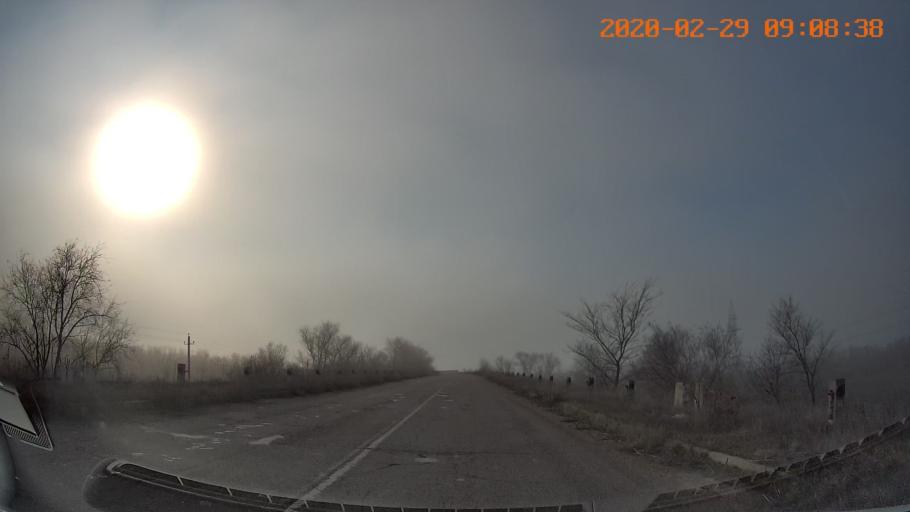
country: MD
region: Telenesti
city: Tiraspolul Nou
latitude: 46.8480
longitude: 29.7534
